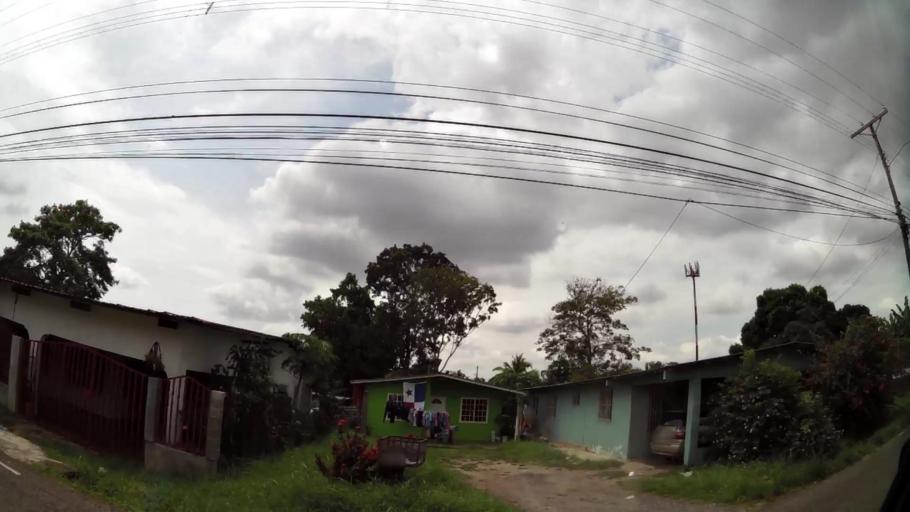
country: PA
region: Panama
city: San Miguelito
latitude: 9.0503
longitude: -79.4246
